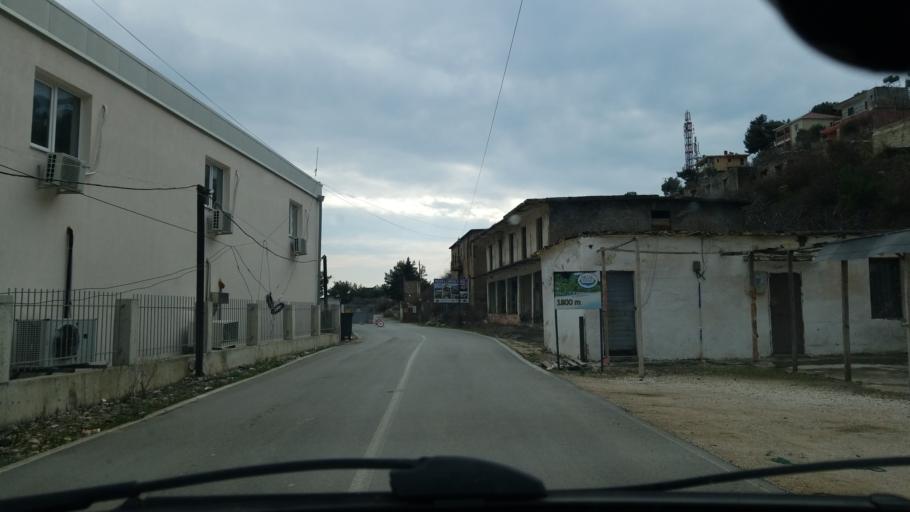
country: AL
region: Lezhe
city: Shengjin
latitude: 41.8143
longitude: 19.5856
